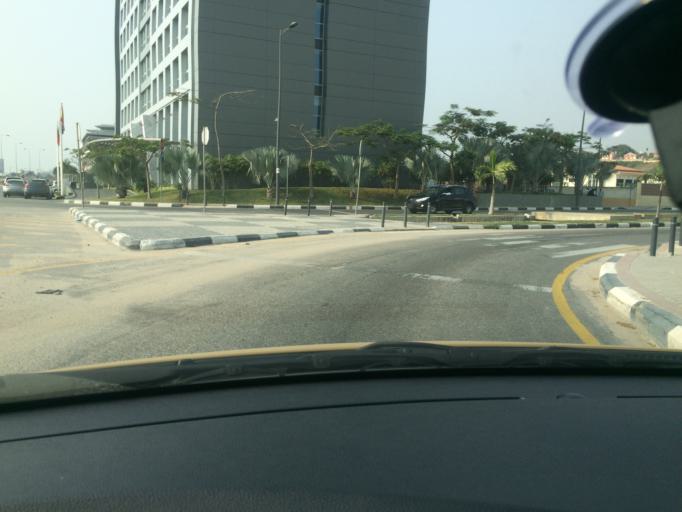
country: AO
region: Luanda
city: Luanda
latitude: -8.8202
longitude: 13.2166
